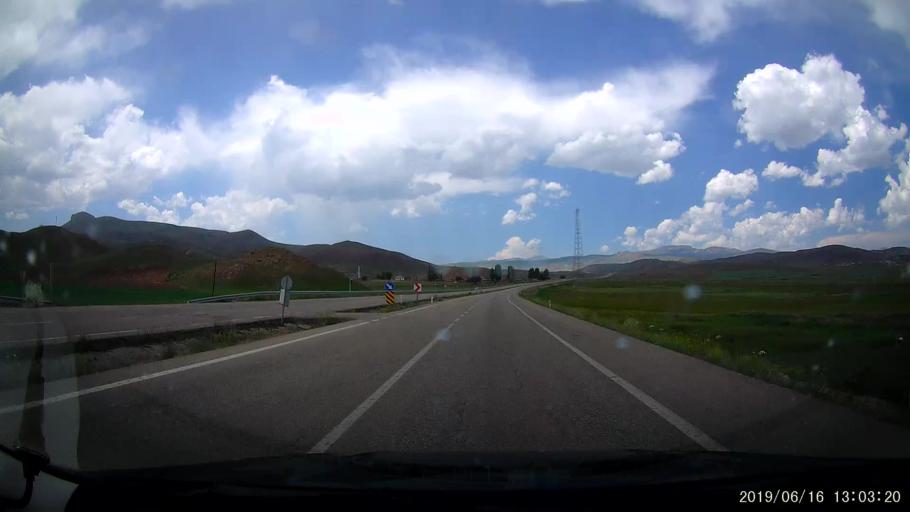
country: TR
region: Agri
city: Sulucem
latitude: 39.5804
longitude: 43.7925
